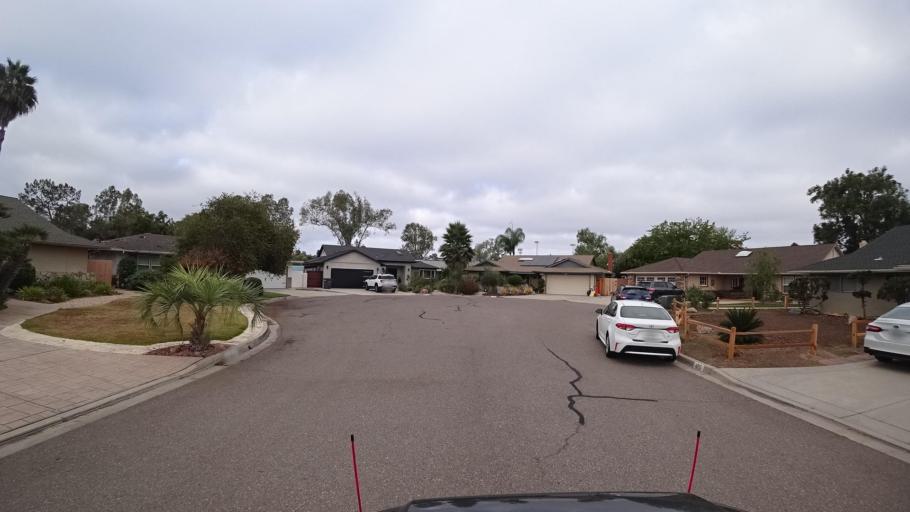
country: US
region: California
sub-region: San Diego County
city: Lake San Marcos
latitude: 33.1294
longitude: -117.2009
